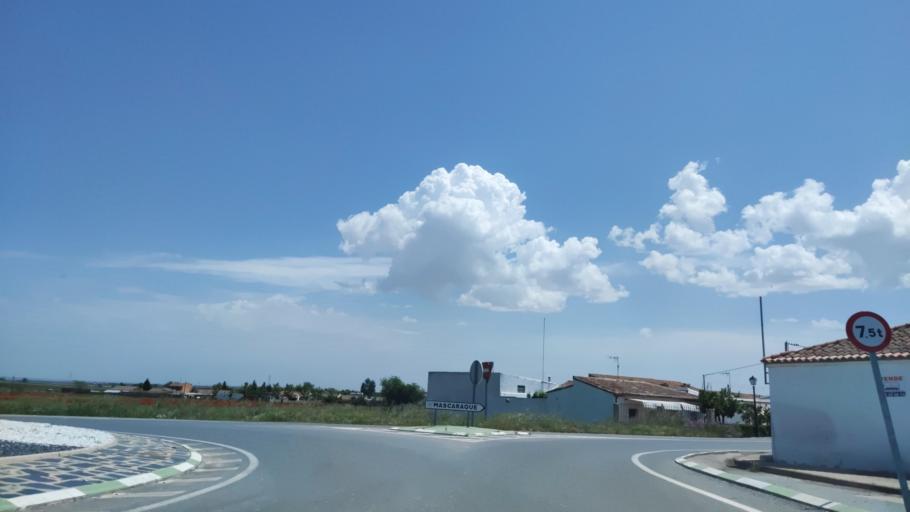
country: ES
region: Castille-La Mancha
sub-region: Province of Toledo
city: Mascaraque
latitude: 39.7189
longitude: -3.8156
